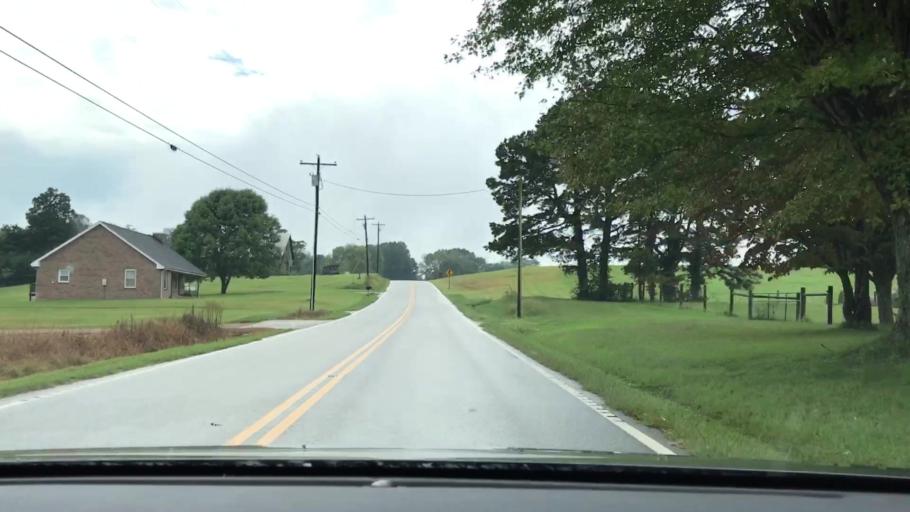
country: US
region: Tennessee
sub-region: Macon County
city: Red Boiling Springs
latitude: 36.4377
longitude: -85.8876
